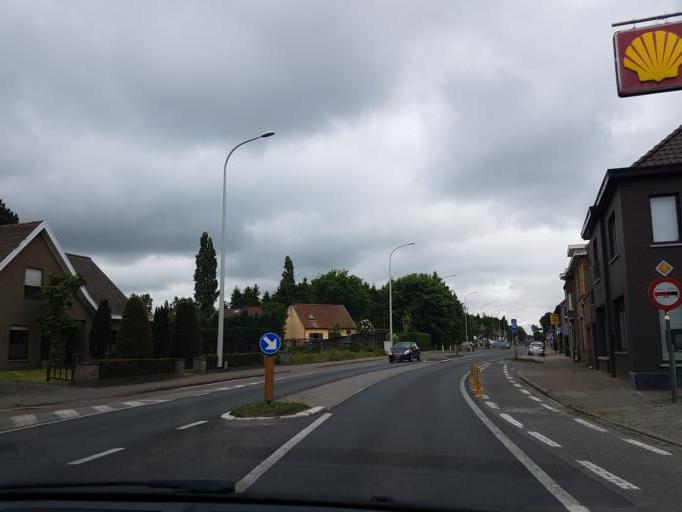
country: BE
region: Flanders
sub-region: Provincie West-Vlaanderen
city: Beernem
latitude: 51.1266
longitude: 3.3281
